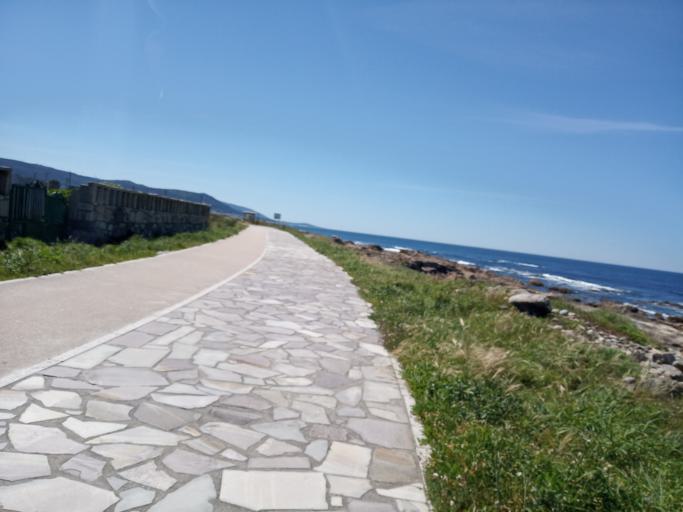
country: ES
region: Galicia
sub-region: Provincia de Pontevedra
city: A Guarda
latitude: 41.8832
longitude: -8.8814
